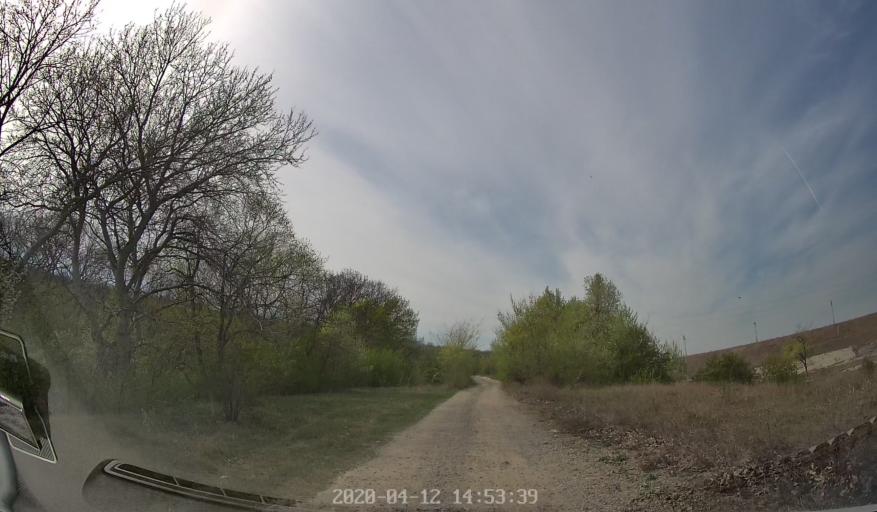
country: MD
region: Telenesti
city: Cocieri
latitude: 47.2748
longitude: 29.1205
